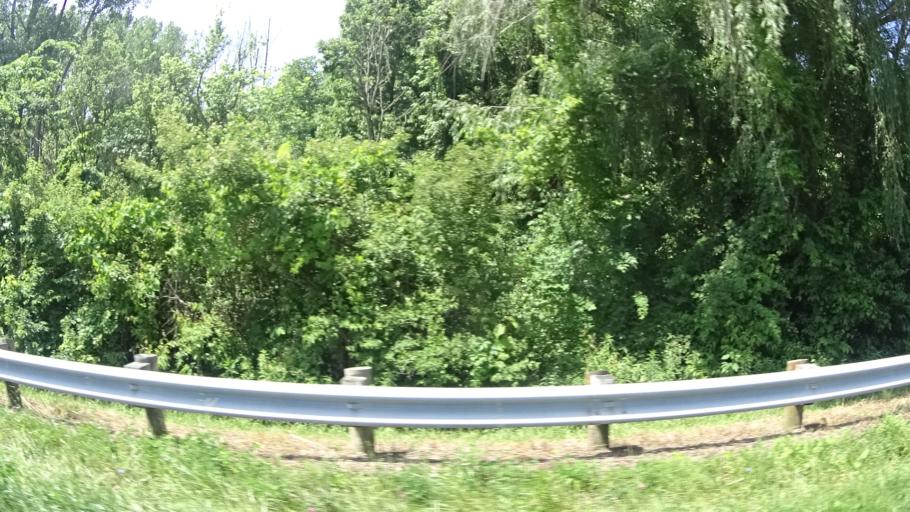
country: US
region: Ohio
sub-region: Erie County
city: Huron
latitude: 41.3499
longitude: -82.5139
